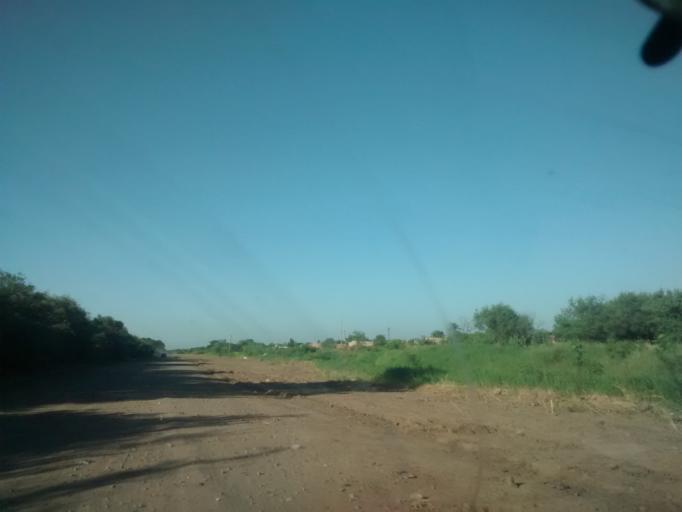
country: AR
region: Chaco
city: Resistencia
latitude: -27.4640
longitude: -59.0295
